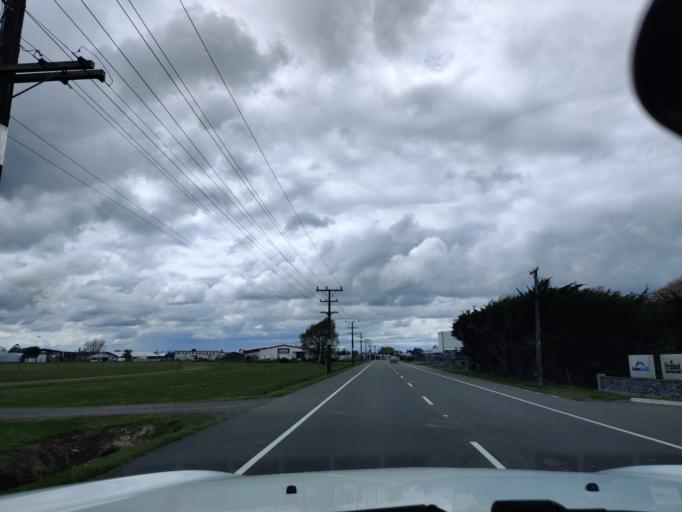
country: NZ
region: Manawatu-Wanganui
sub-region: Palmerston North City
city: Palmerston North
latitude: -40.2334
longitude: 175.5657
